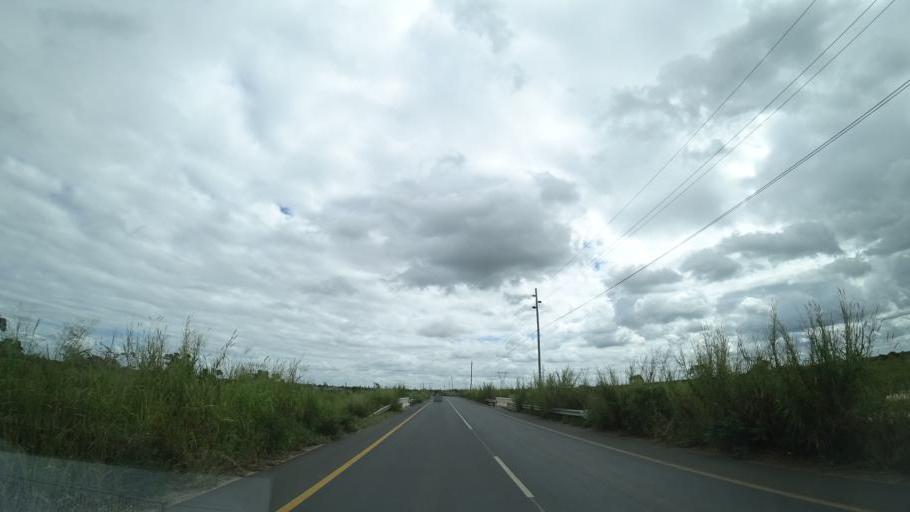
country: MZ
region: Sofala
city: Dondo
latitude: -19.5175
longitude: 34.6200
